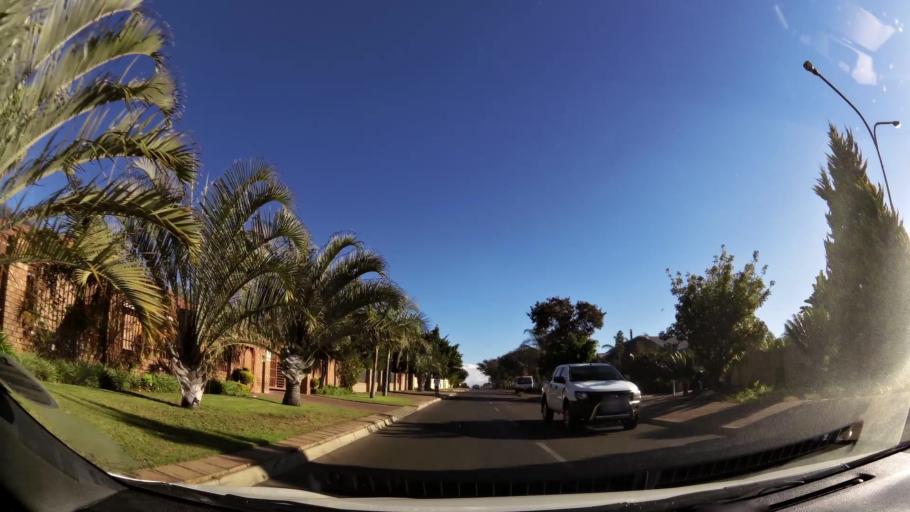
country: ZA
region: Limpopo
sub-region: Capricorn District Municipality
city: Polokwane
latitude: -23.8812
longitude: 29.4893
